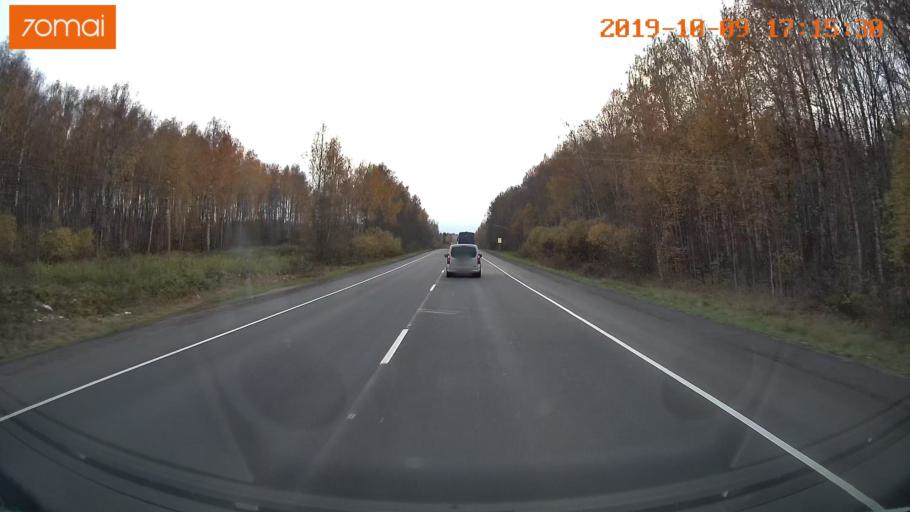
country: RU
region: Ivanovo
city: Furmanov
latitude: 57.2972
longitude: 41.1888
